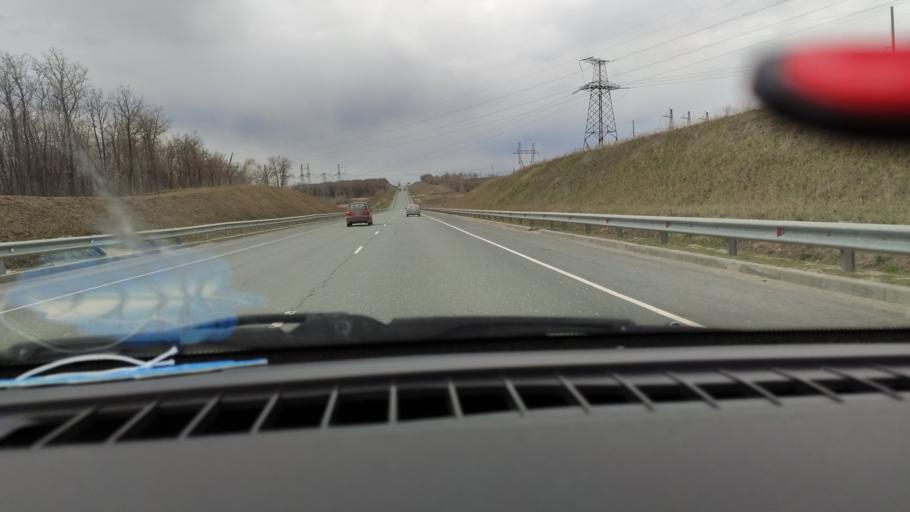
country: RU
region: Saratov
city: Yelshanka
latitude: 51.8233
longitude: 46.3163
